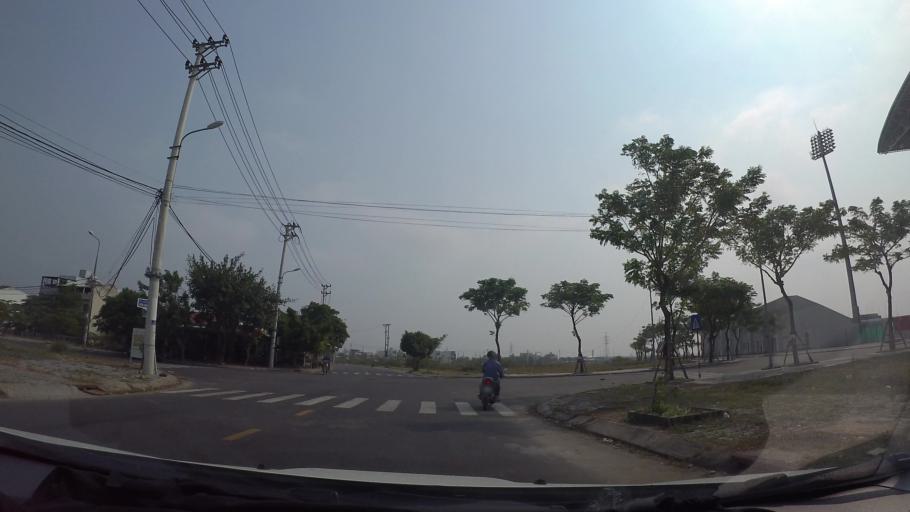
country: VN
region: Da Nang
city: Cam Le
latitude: 16.0001
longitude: 108.2222
